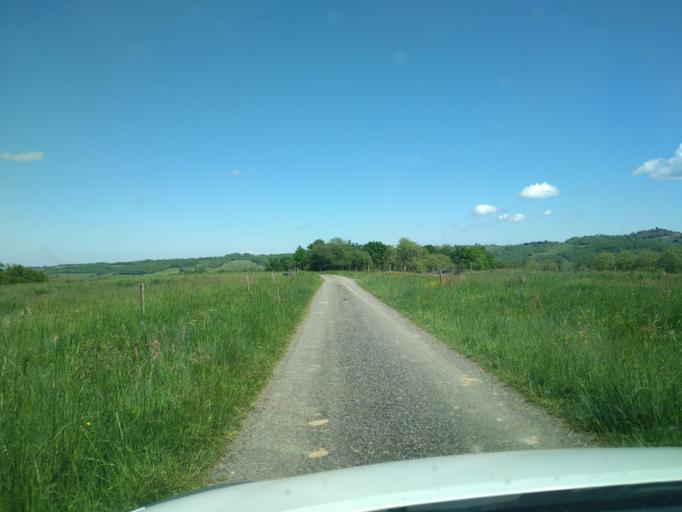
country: FR
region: Midi-Pyrenees
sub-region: Departement de la Haute-Garonne
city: Boulogne-sur-Gesse
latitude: 43.3016
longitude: 0.6665
